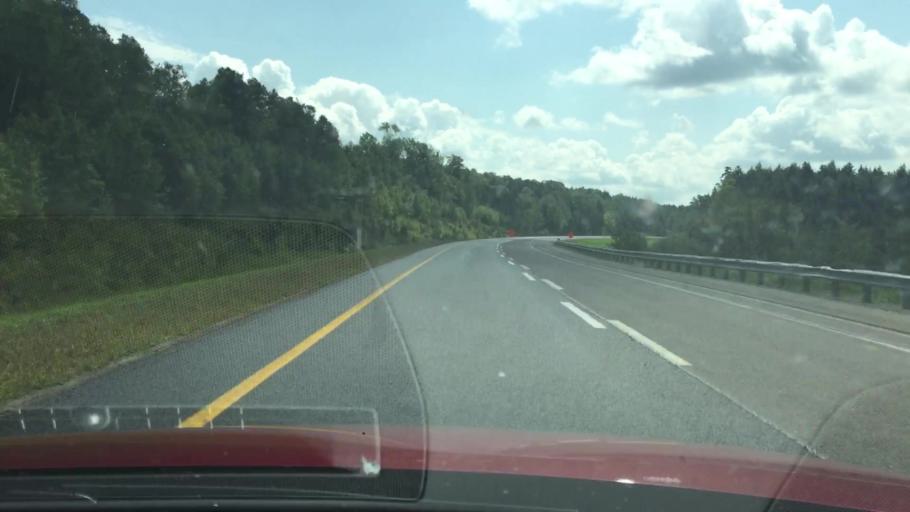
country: US
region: Maine
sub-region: Penobscot County
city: Medway
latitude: 45.7130
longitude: -68.4760
